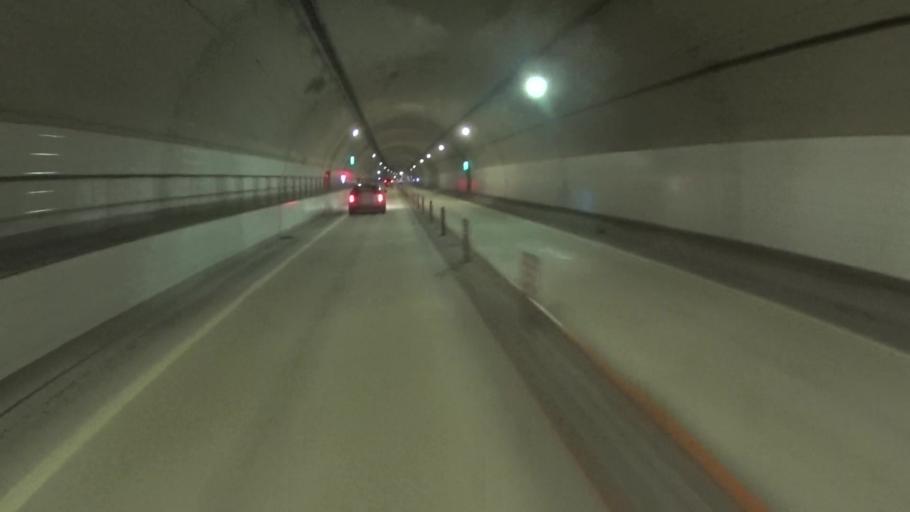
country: JP
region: Kyoto
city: Miyazu
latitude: 35.5265
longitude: 135.1764
